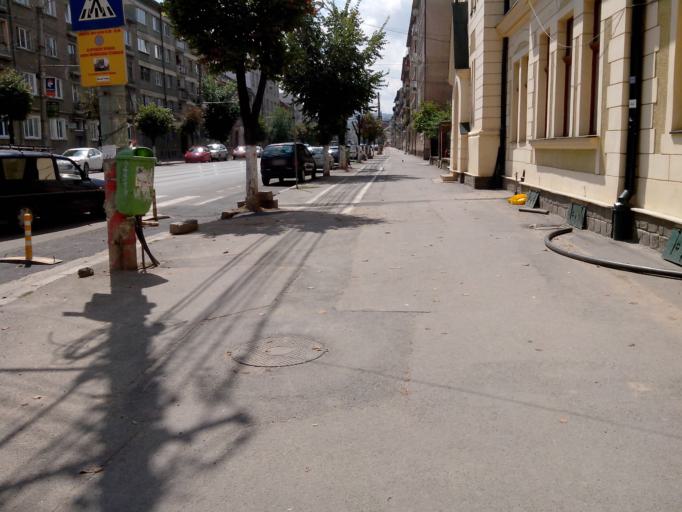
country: RO
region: Cluj
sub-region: Municipiul Cluj-Napoca
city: Cluj-Napoca
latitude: 46.7805
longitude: 23.5875
